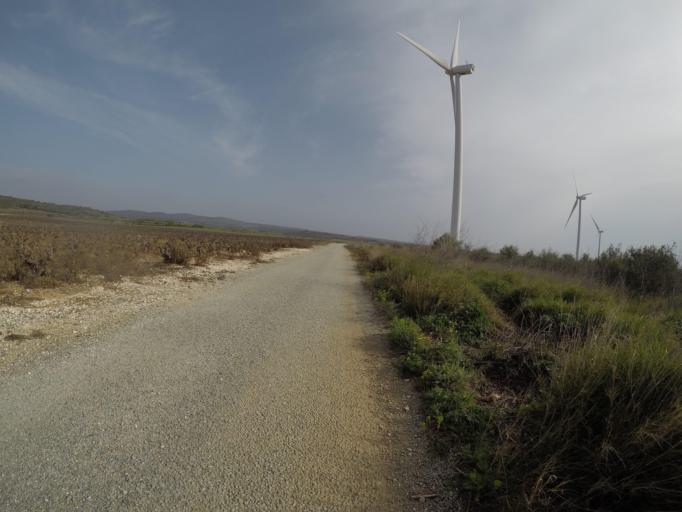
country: FR
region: Languedoc-Roussillon
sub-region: Departement des Pyrenees-Orientales
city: Pezilla-la-Riviere
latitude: 42.7280
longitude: 2.7815
